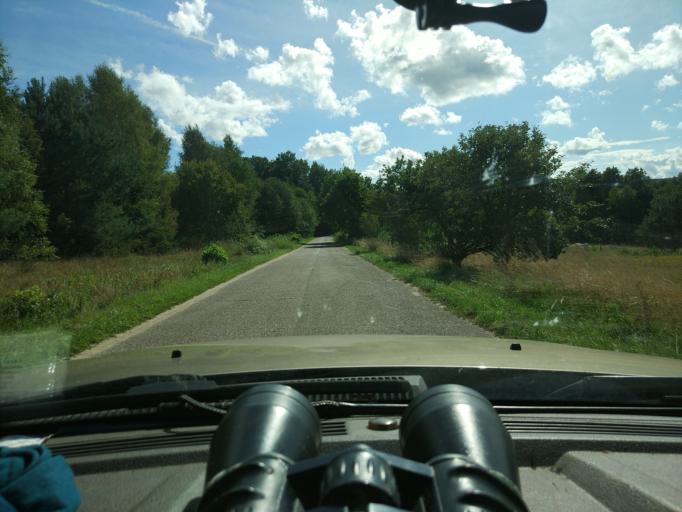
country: PL
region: Pomeranian Voivodeship
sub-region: Powiat wejherowski
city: Choczewo
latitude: 54.7621
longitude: 17.7924
